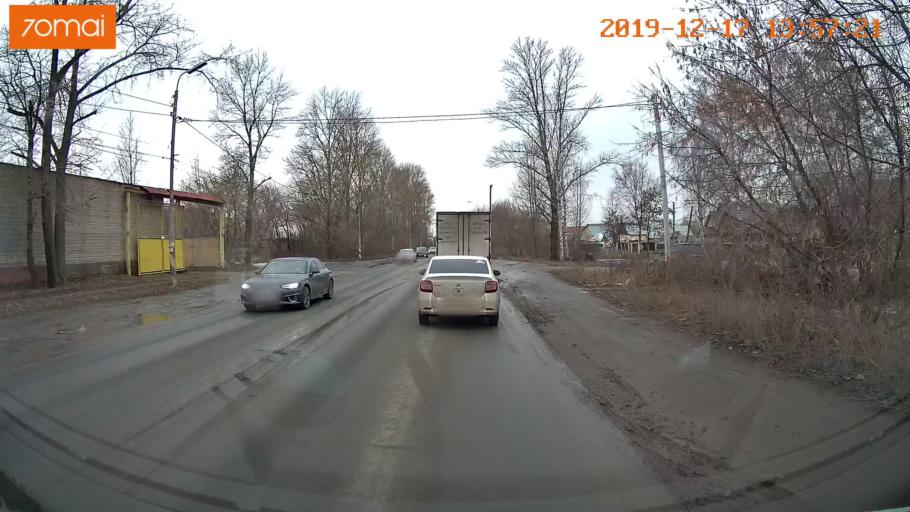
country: RU
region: Rjazan
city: Ryazan'
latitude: 54.6258
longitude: 39.6906
